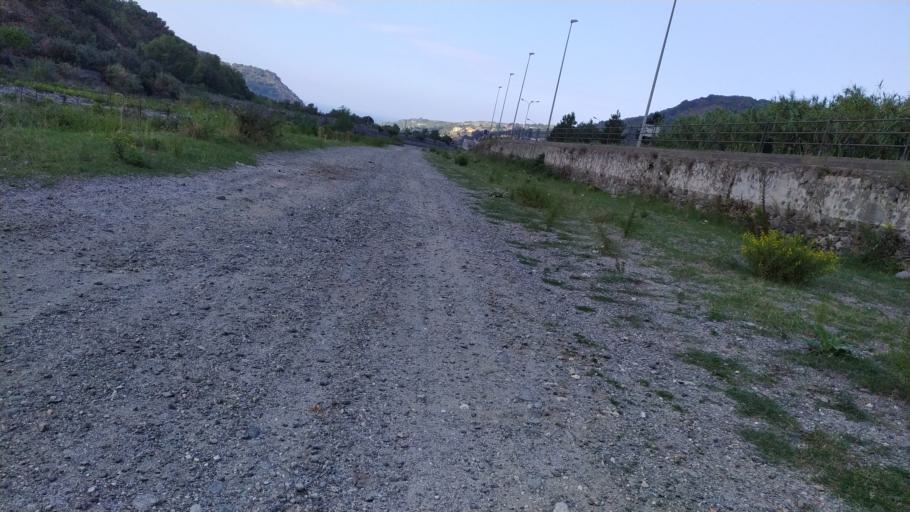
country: IT
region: Sicily
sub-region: Messina
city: Saponara
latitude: 38.1976
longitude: 15.4298
